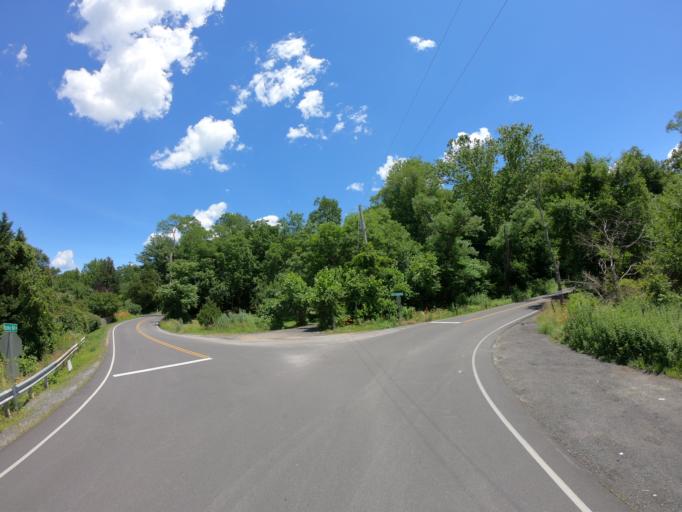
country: US
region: Delaware
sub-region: New Castle County
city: Middletown
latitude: 39.4653
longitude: -75.7753
